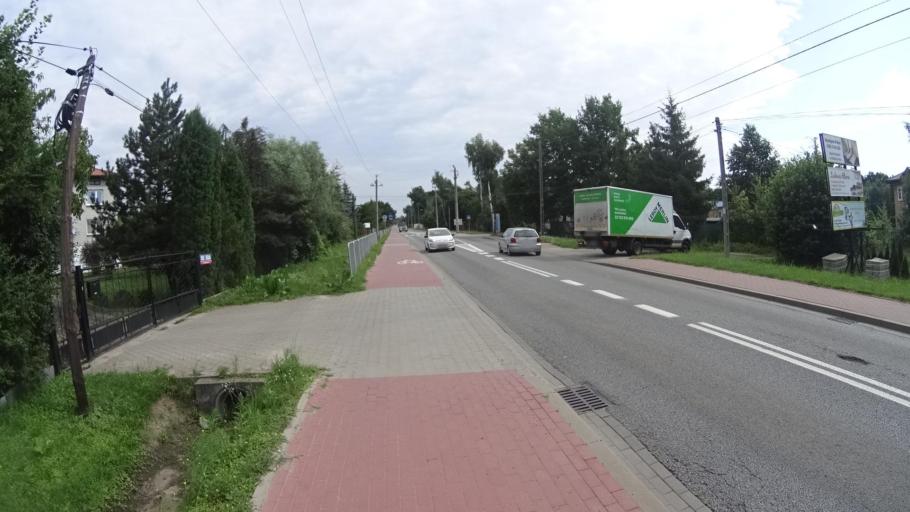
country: PL
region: Masovian Voivodeship
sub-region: Powiat pruszkowski
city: Nadarzyn
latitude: 52.0857
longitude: 20.7954
